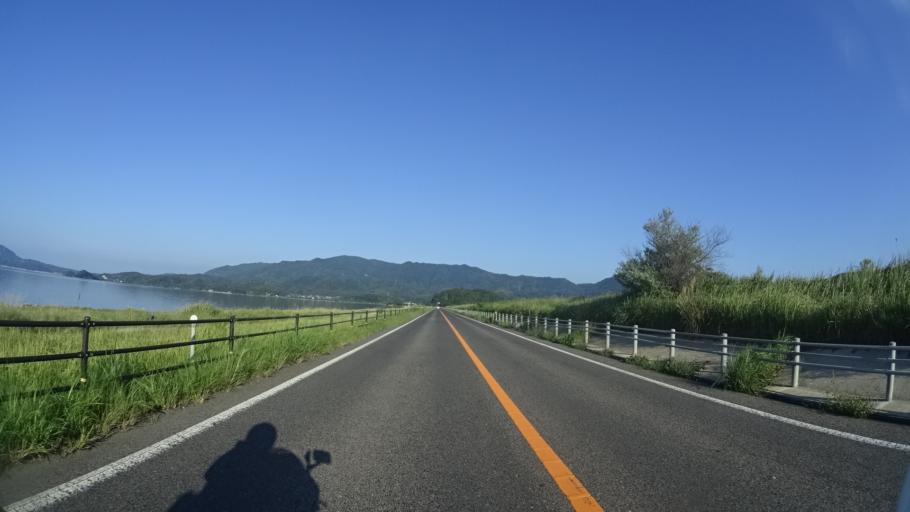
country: JP
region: Shimane
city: Sakaiminato
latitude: 35.5281
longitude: 133.1709
